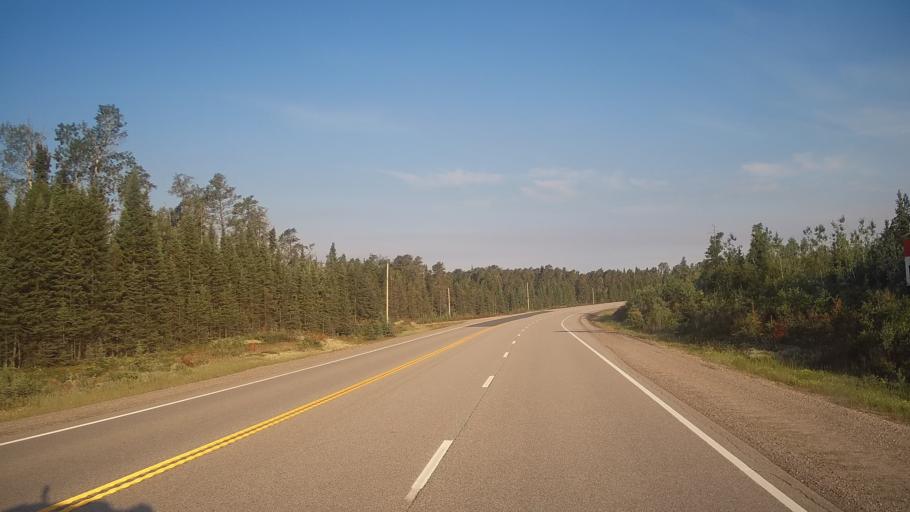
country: CA
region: Ontario
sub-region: Rainy River District
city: Atikokan
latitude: 49.3714
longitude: -91.5676
